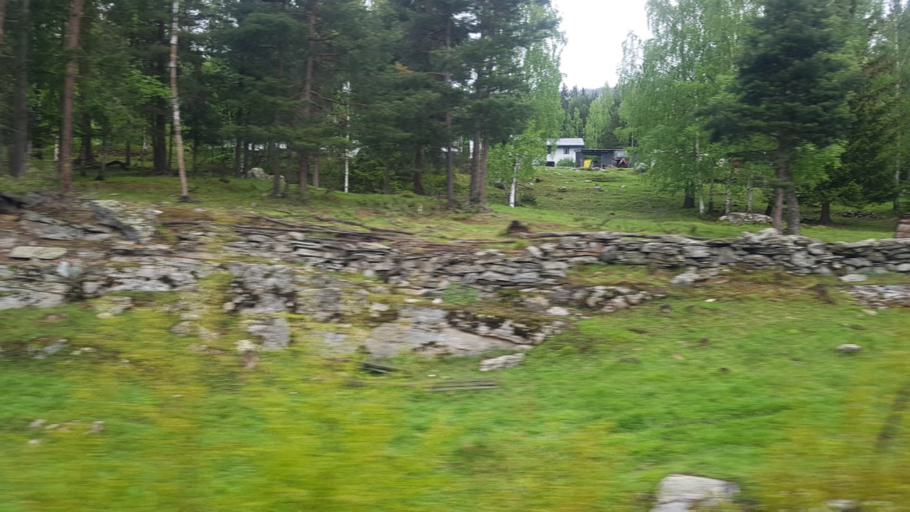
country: NO
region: Oppland
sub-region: Sor-Fron
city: Hundorp
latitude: 61.5557
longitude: 9.9437
